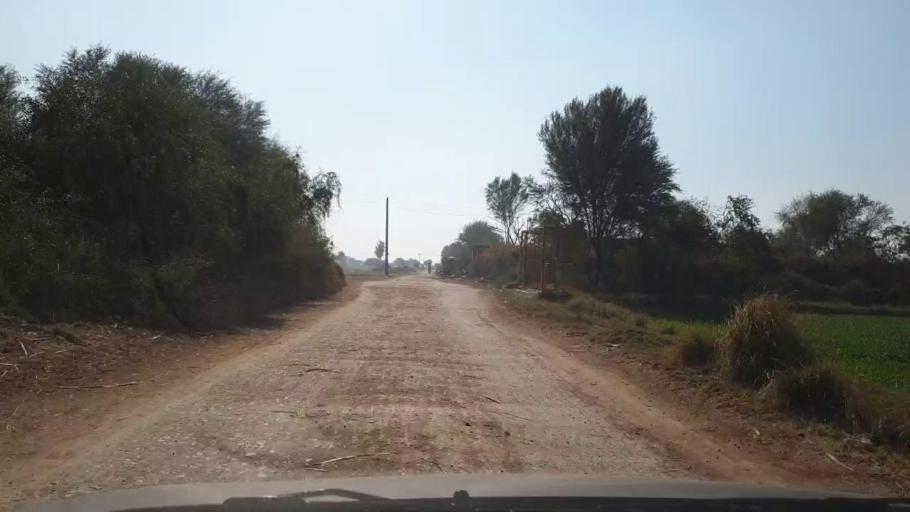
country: PK
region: Sindh
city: Jhol
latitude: 25.9385
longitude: 68.7999
